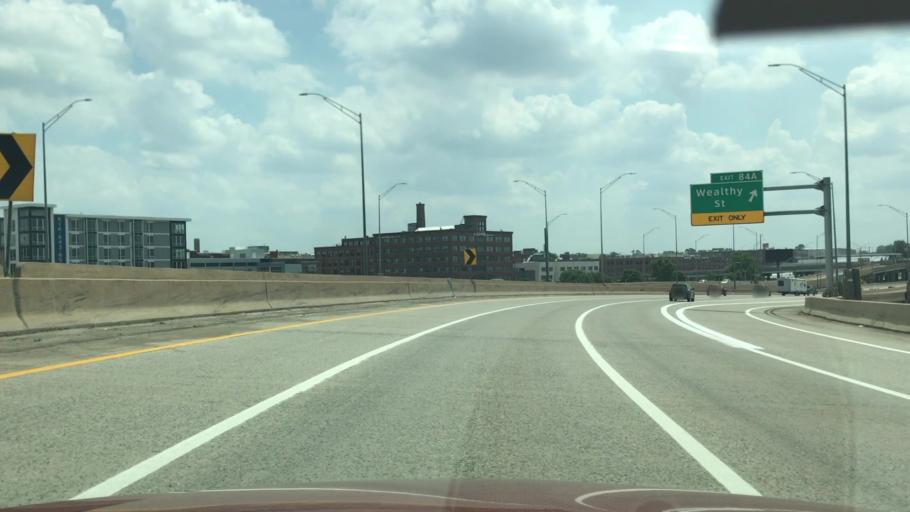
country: US
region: Michigan
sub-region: Kent County
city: Grand Rapids
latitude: 42.9595
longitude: -85.6722
